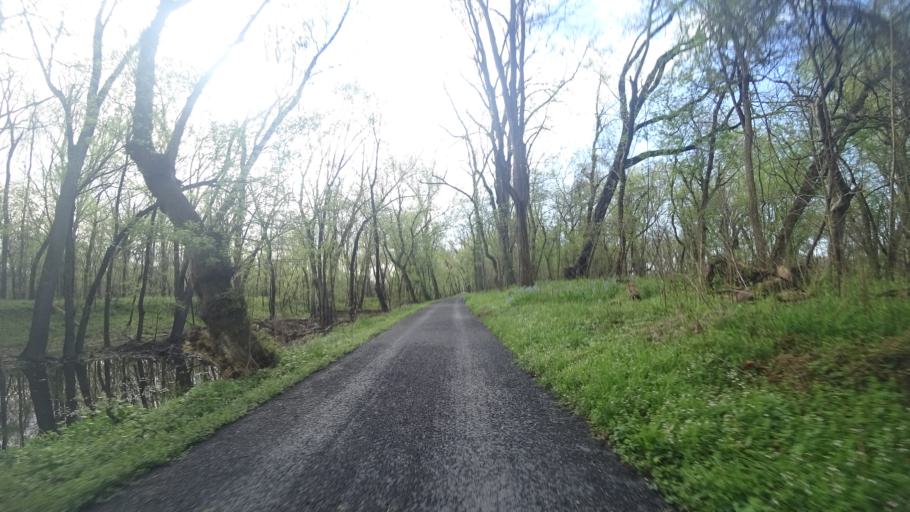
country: US
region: Virginia
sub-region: Loudoun County
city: University Center
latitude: 39.0912
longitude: -77.4646
